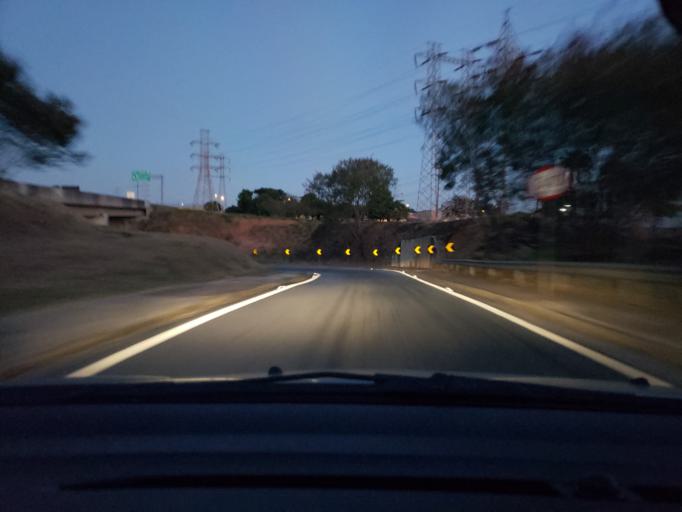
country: BR
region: Sao Paulo
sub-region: Campinas
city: Campinas
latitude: -22.9184
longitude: -47.0959
